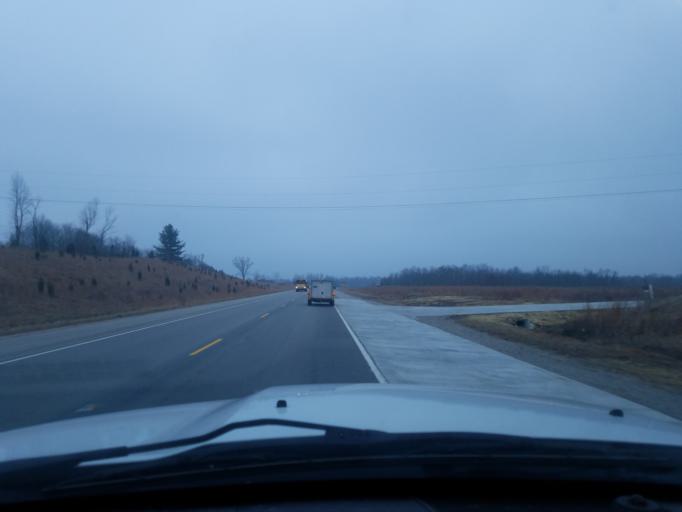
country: US
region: Indiana
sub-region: Perry County
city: Tell City
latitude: 38.0658
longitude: -86.6199
